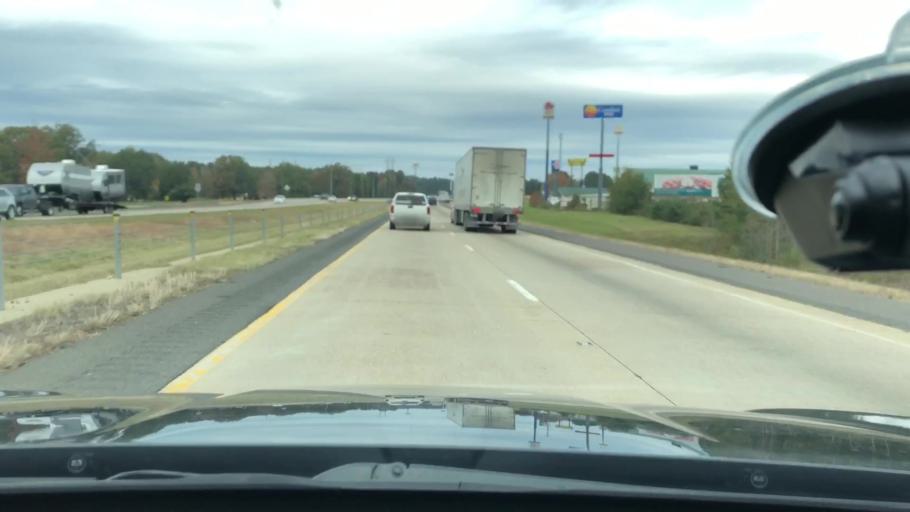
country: US
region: Arkansas
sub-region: Clark County
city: Arkadelphia
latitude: 34.1789
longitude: -93.0736
